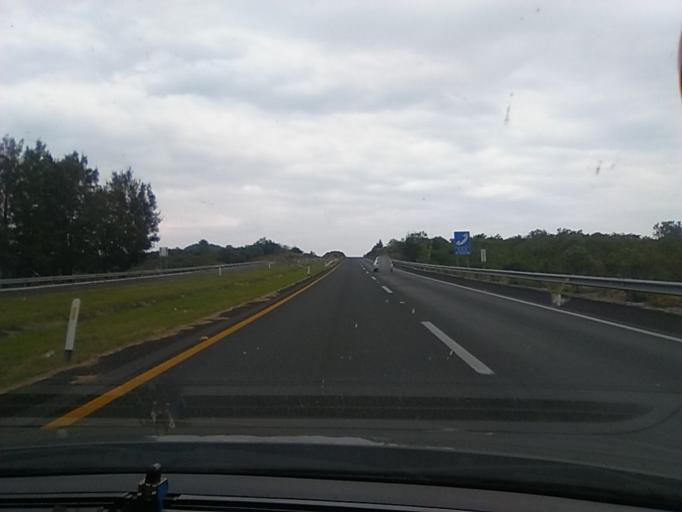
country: MX
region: Michoacan
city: Penjamillo de Degollado
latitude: 20.0023
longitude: -101.8892
